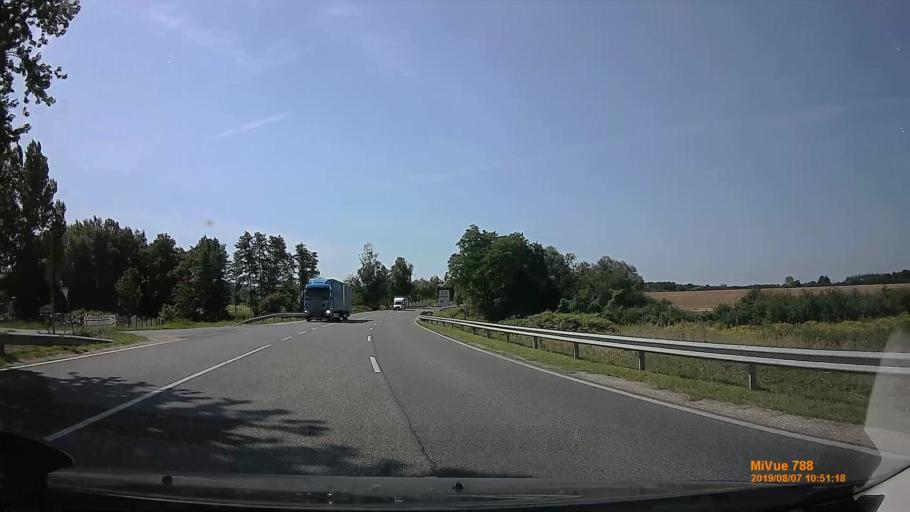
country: SI
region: Lendava-Lendva
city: Lendava
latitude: 46.6047
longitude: 16.4635
